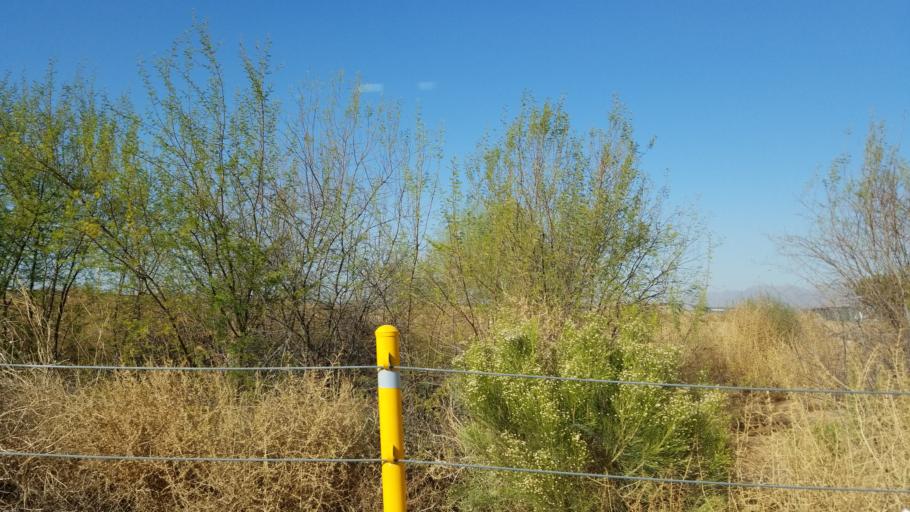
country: US
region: Arizona
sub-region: Maricopa County
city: Scottsdale
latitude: 33.5142
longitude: -111.8801
